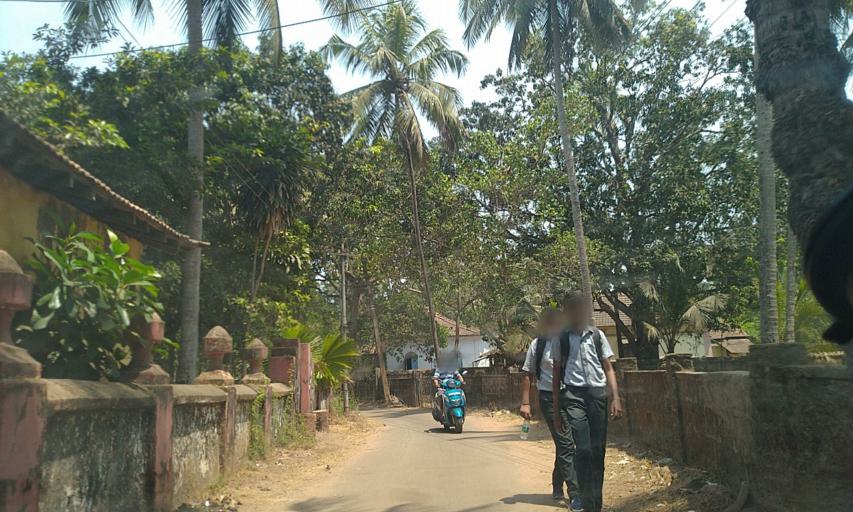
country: IN
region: Goa
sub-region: North Goa
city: Saligao
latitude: 15.5507
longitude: 73.7874
